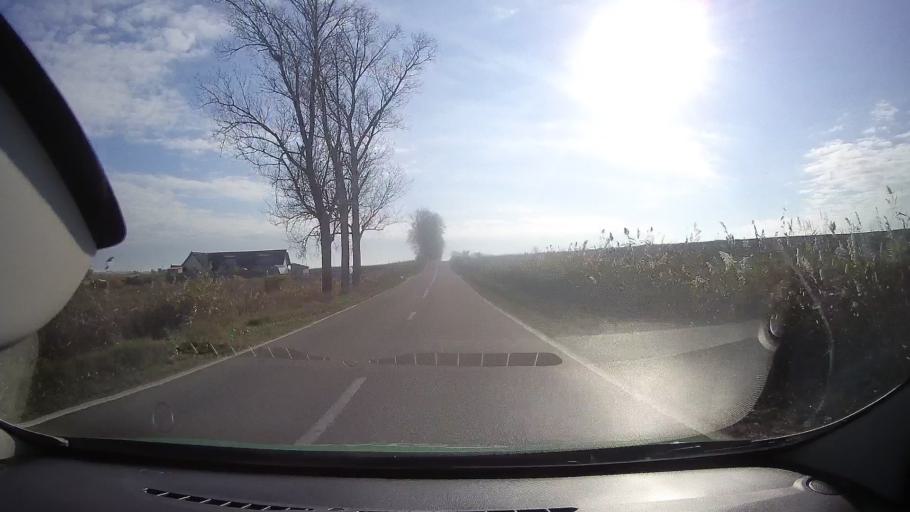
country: RO
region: Tulcea
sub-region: Comuna Mahmudia
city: Mahmudia
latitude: 45.0634
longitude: 29.1112
